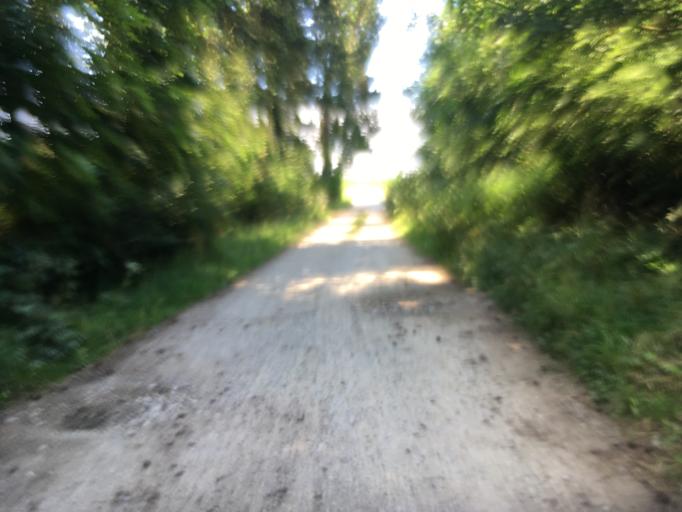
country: CH
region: Fribourg
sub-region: Broye District
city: Domdidier
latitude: 46.9325
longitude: 6.9901
